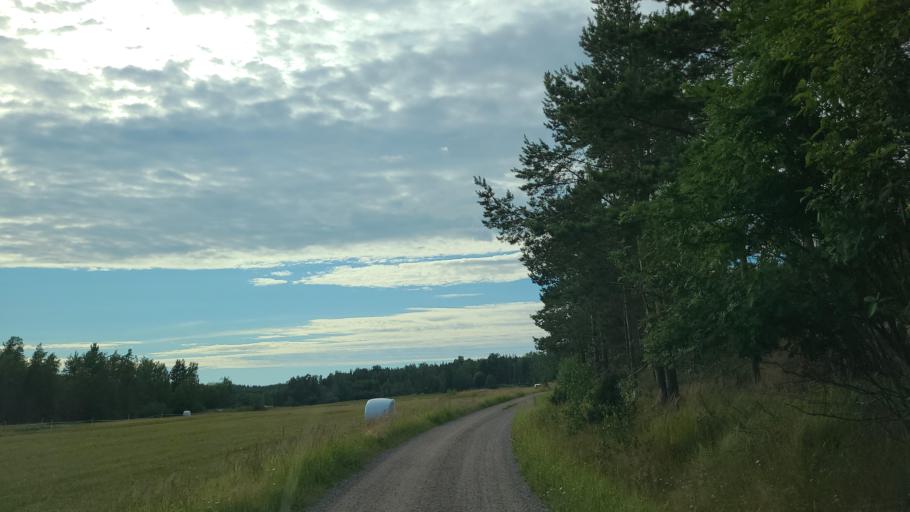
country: FI
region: Varsinais-Suomi
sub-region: Aboland-Turunmaa
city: Nagu
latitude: 60.2816
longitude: 21.9413
